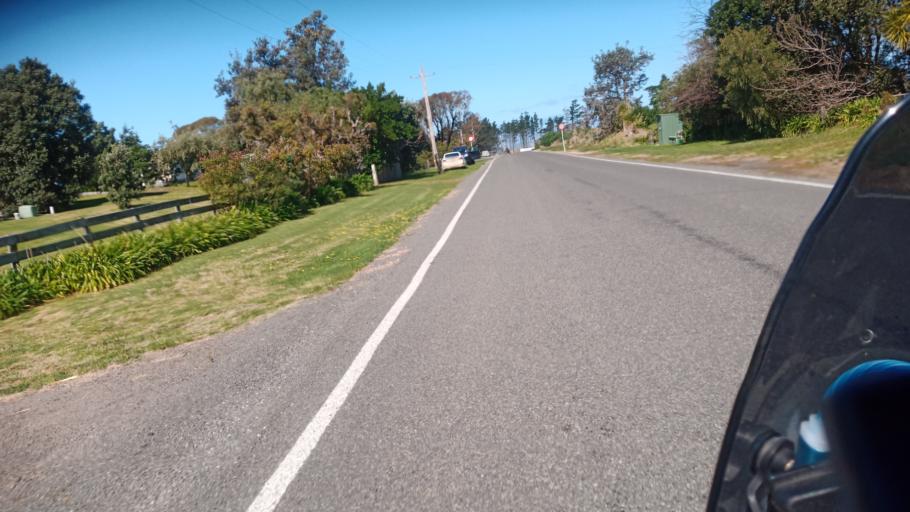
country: NZ
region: Gisborne
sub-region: Gisborne District
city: Gisborne
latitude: -39.0167
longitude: 177.8812
